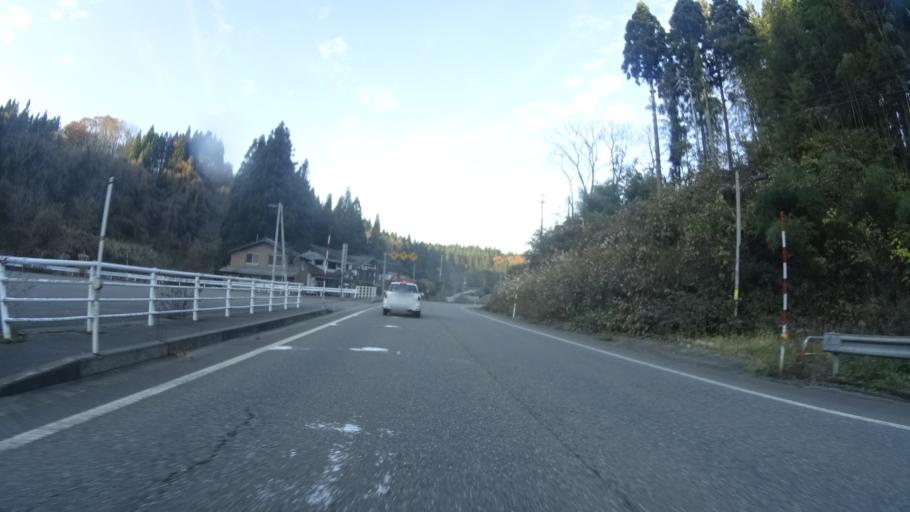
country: JP
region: Niigata
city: Ojiya
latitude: 37.4112
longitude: 138.7034
